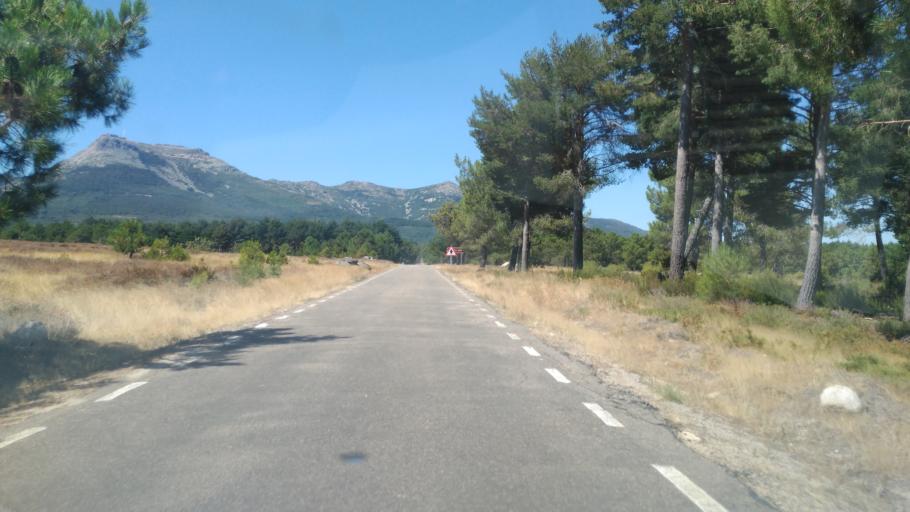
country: ES
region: Castille and Leon
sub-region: Provincia de Salamanca
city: Nava de Francia
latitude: 40.5237
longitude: -6.1160
